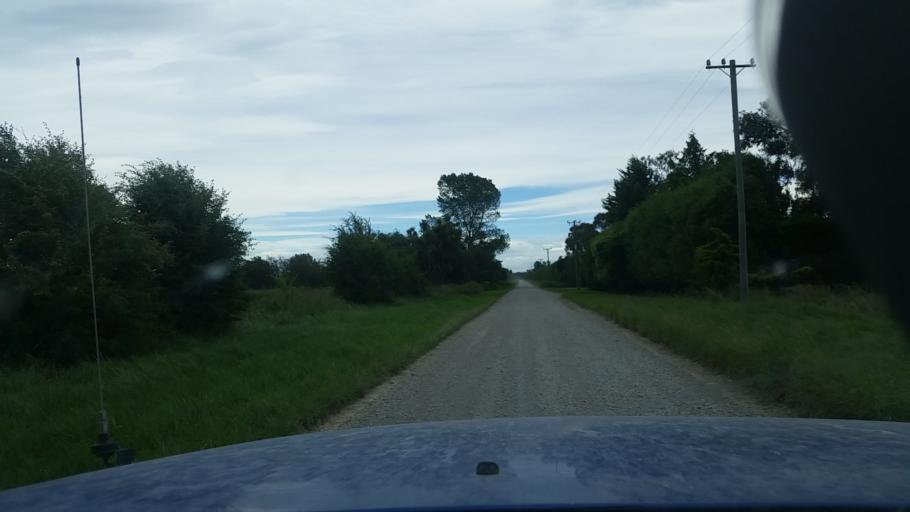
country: NZ
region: Canterbury
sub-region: Ashburton District
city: Ashburton
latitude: -43.8443
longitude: 171.6591
